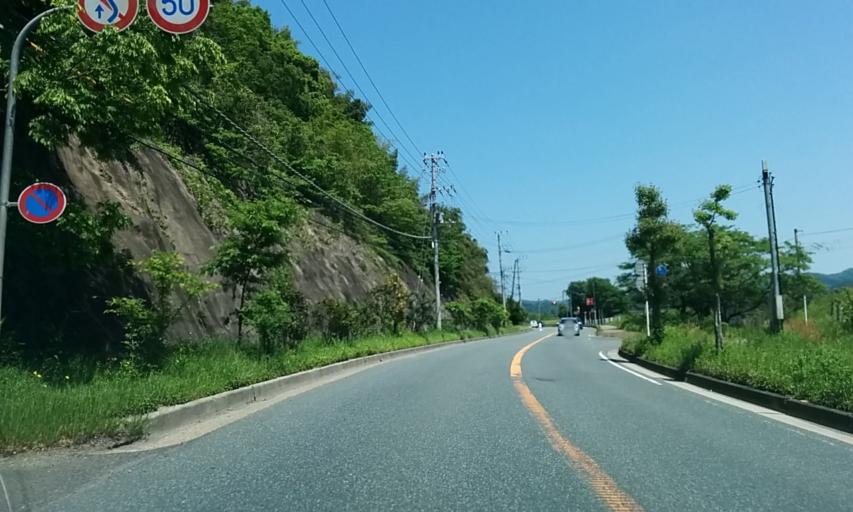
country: JP
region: Kyoto
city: Fukuchiyama
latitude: 35.3825
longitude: 135.1392
